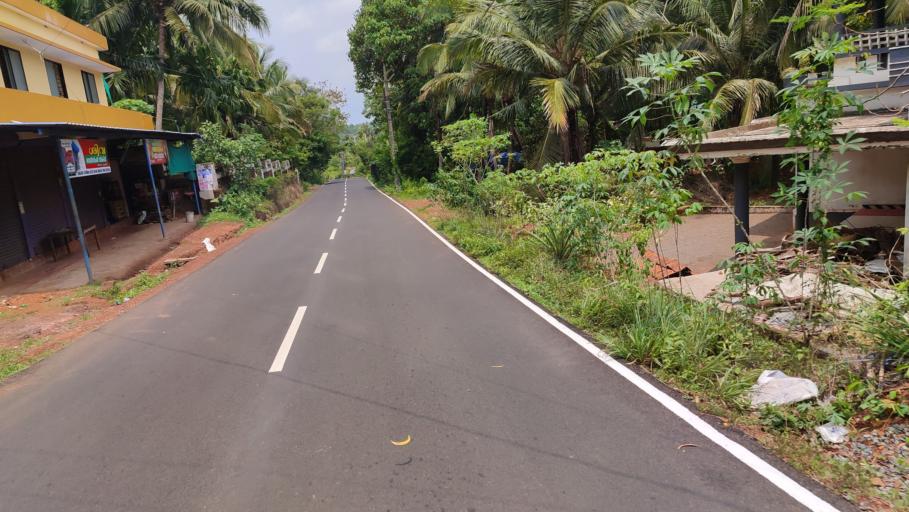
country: IN
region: Kerala
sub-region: Kasaragod District
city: Kannangad
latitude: 12.3219
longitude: 75.1350
